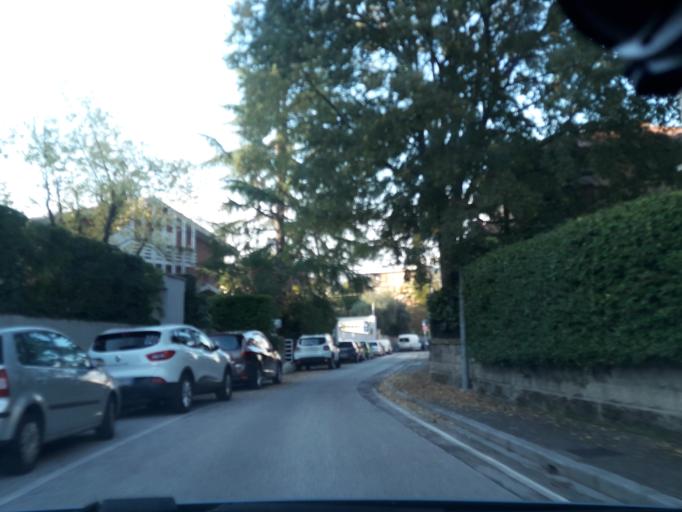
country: IT
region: Friuli Venezia Giulia
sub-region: Provincia di Udine
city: Udine
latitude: 46.0741
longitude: 13.2362
